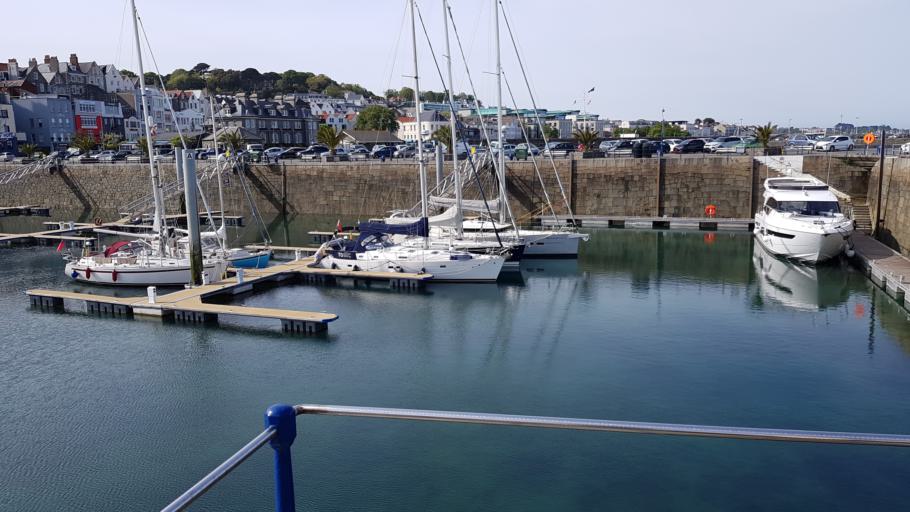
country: GG
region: St Peter Port
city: Saint Peter Port
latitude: 49.4554
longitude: -2.5340
